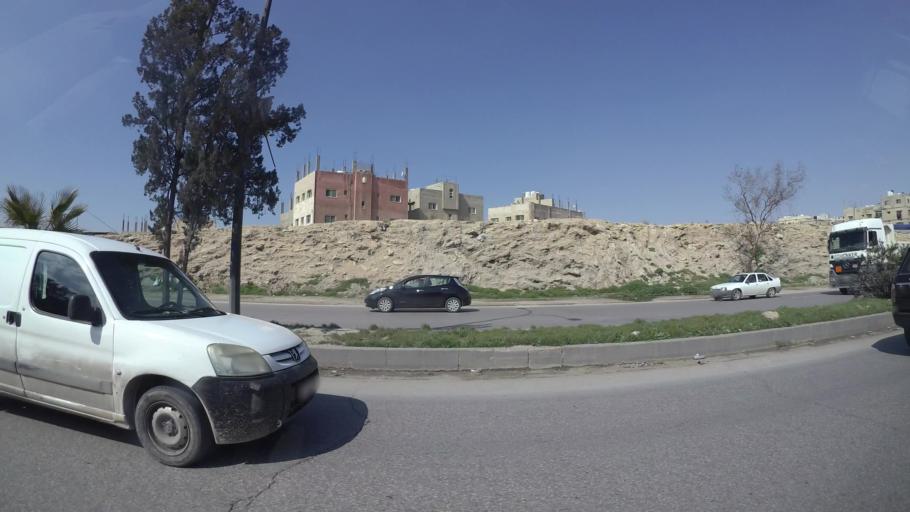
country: JO
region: Zarqa
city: Russeifa
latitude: 31.9961
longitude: 36.0270
